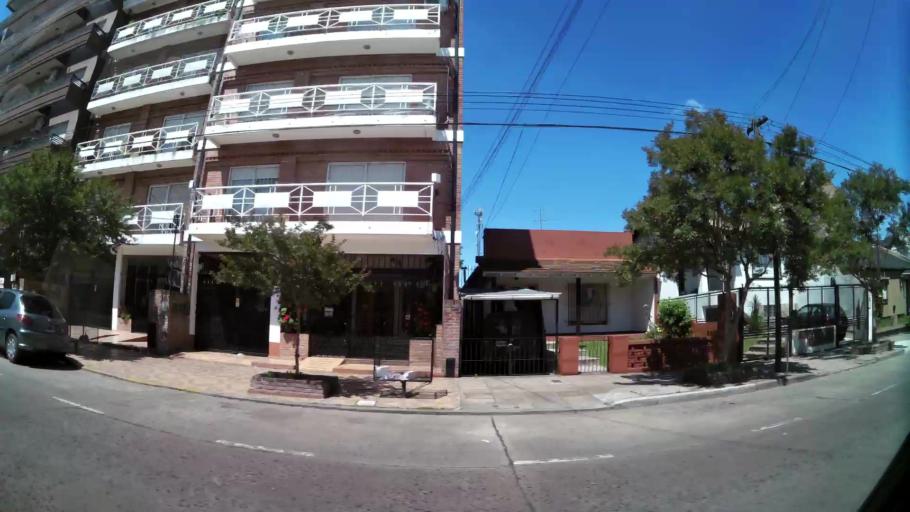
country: AR
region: Buenos Aires
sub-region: Partido de Tigre
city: Tigre
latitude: -34.4253
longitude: -58.5734
